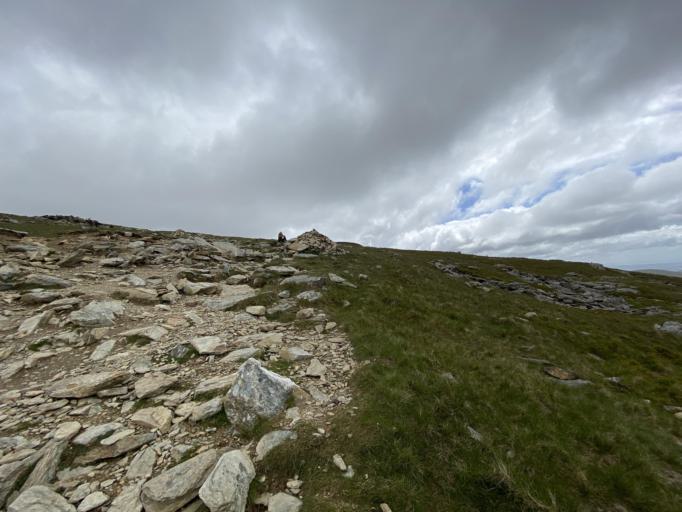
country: GB
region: Wales
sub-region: Gwynedd
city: Llanberis
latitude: 53.0631
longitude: -4.0980
